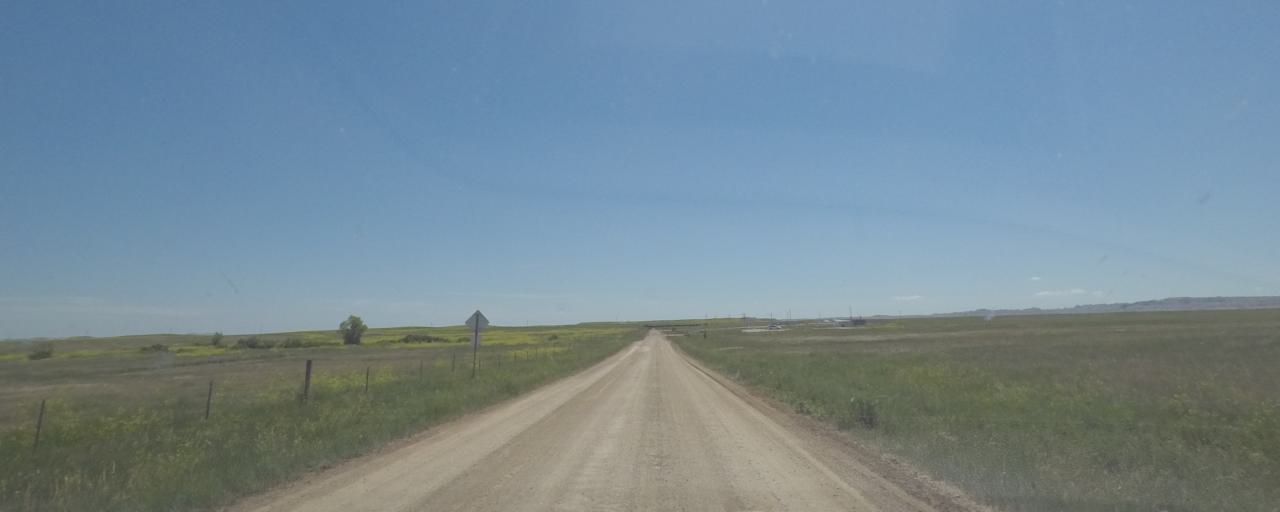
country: US
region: South Dakota
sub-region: Haakon County
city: Philip
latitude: 43.9352
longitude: -102.1587
